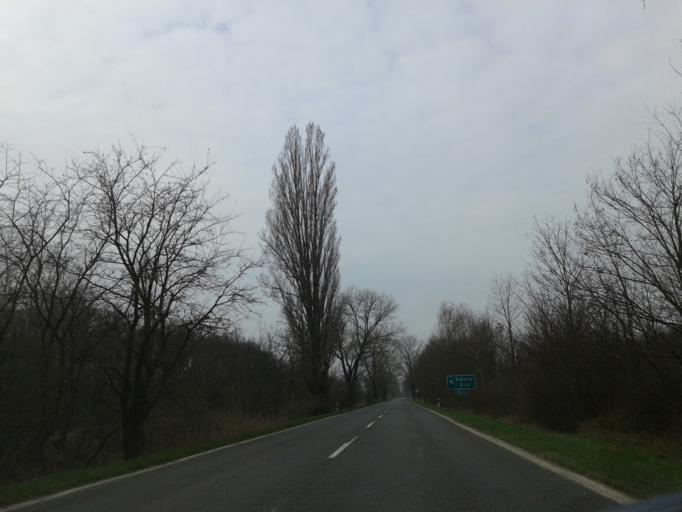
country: HU
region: Komarom-Esztergom
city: Acs
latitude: 47.7243
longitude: 18.0430
